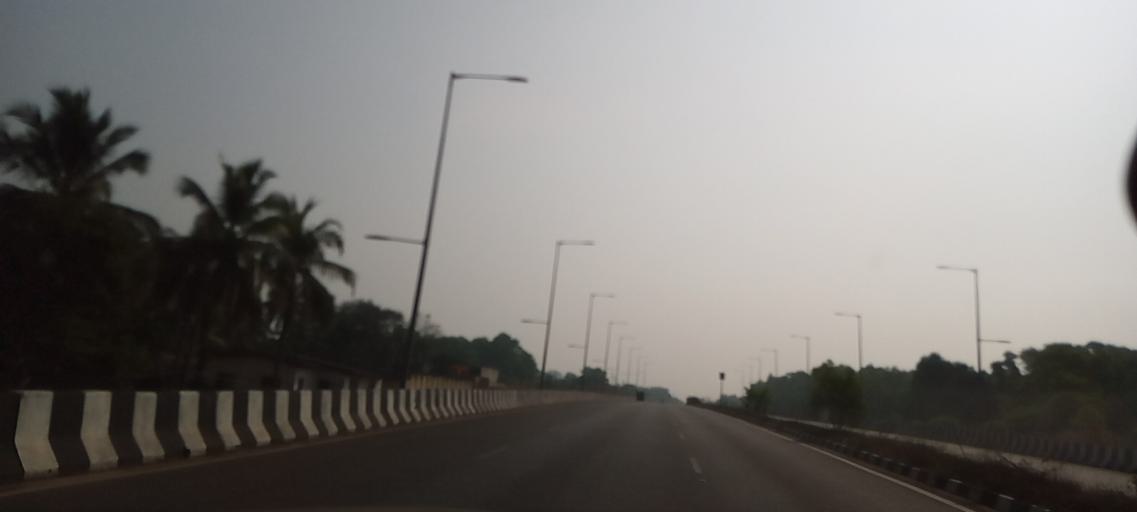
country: IN
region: Karnataka
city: Gangolli
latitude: 13.6881
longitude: 74.6591
